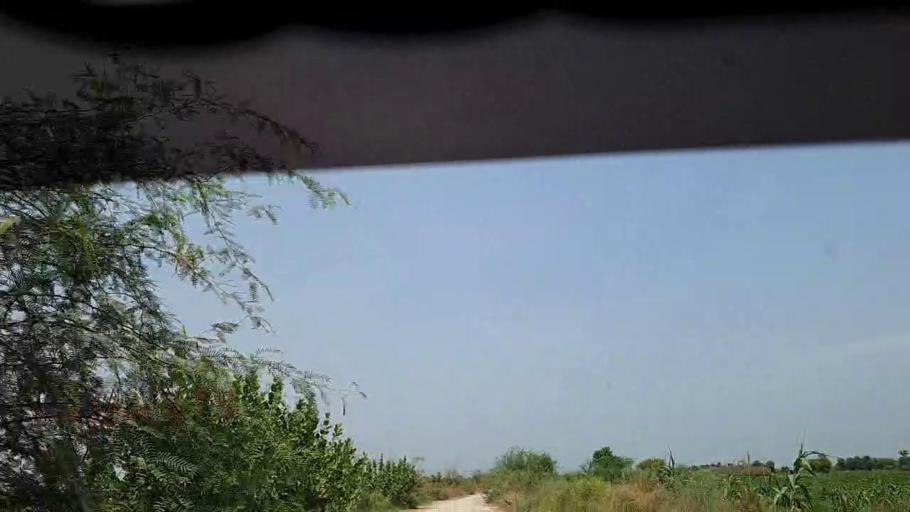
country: PK
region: Sindh
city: Adilpur
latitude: 27.8841
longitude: 69.2587
